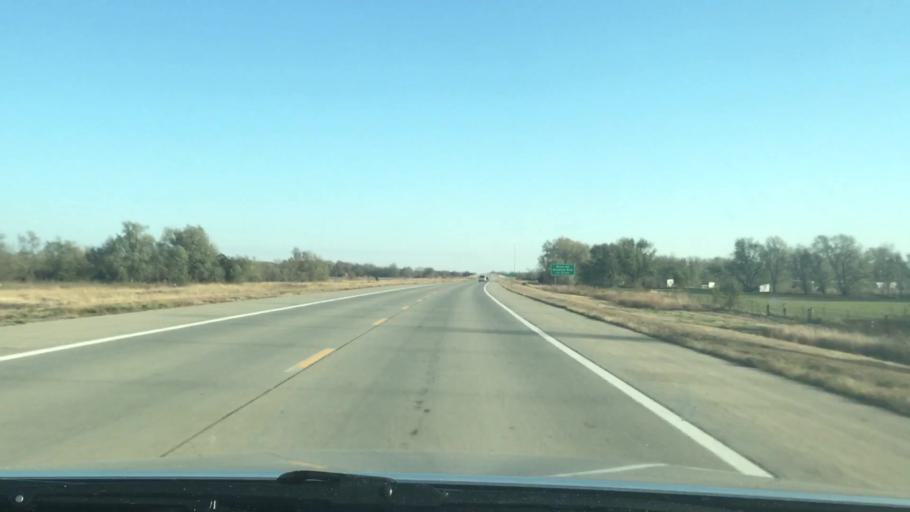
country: US
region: Kansas
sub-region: Reno County
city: Hutchinson
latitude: 38.0996
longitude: -98.0091
